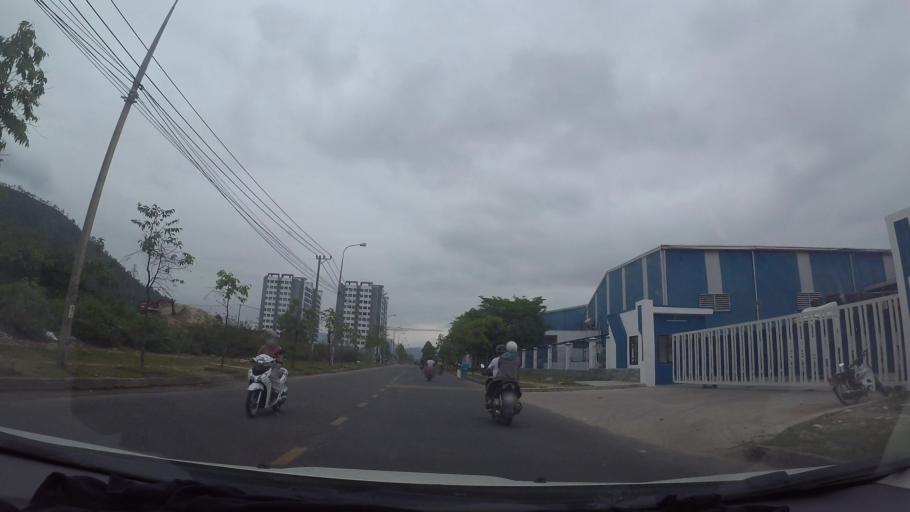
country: VN
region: Da Nang
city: Lien Chieu
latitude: 16.0736
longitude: 108.1380
